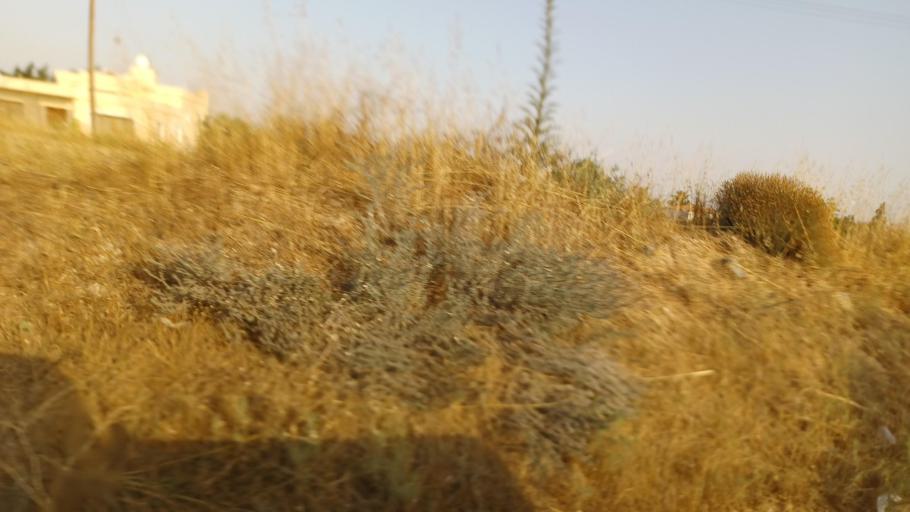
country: CY
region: Ammochostos
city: Paralimni
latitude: 35.0307
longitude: 33.9785
